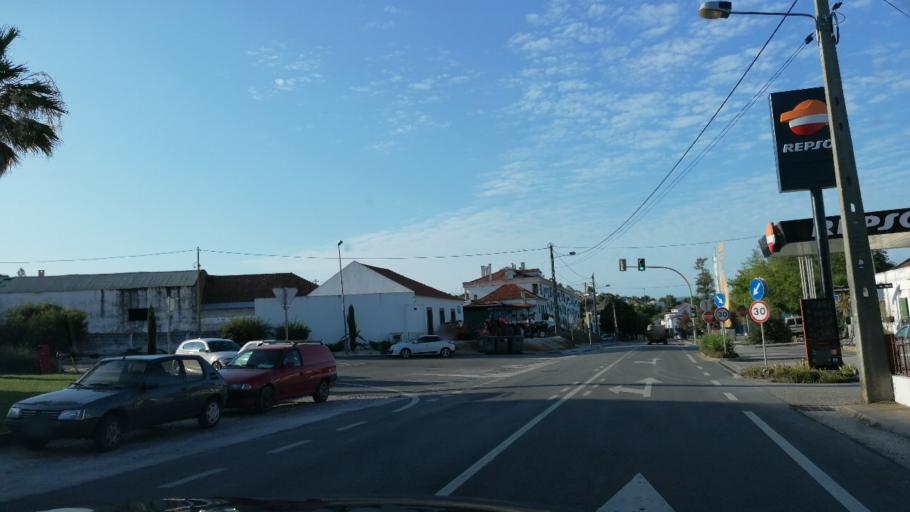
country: PT
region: Santarem
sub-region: Alcanena
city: Alcanena
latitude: 39.3768
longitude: -8.6610
